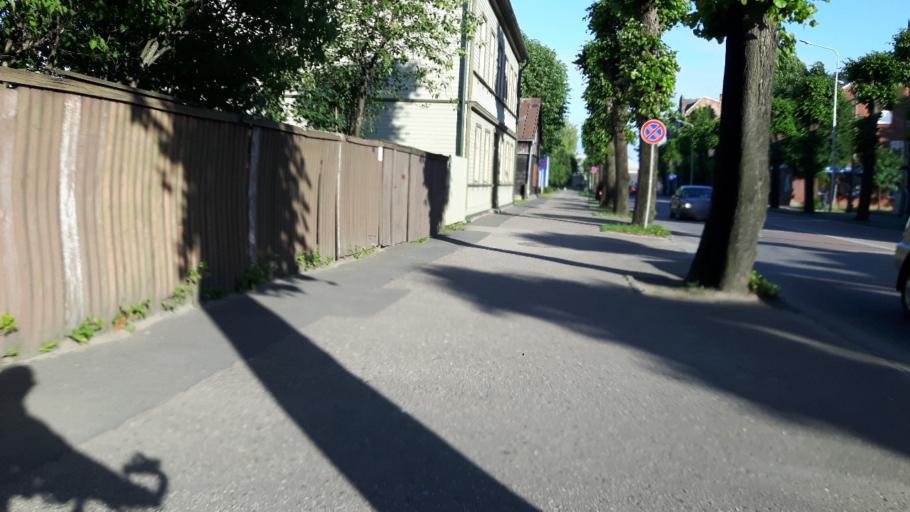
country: LV
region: Liepaja
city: Liepaja
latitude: 56.5164
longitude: 21.0129
